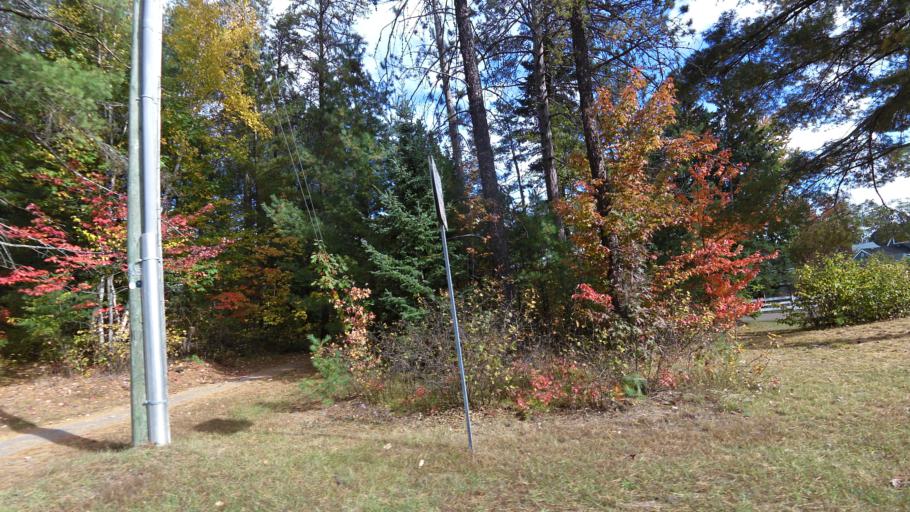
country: CA
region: Ontario
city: Deep River
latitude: 46.0962
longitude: -77.4864
